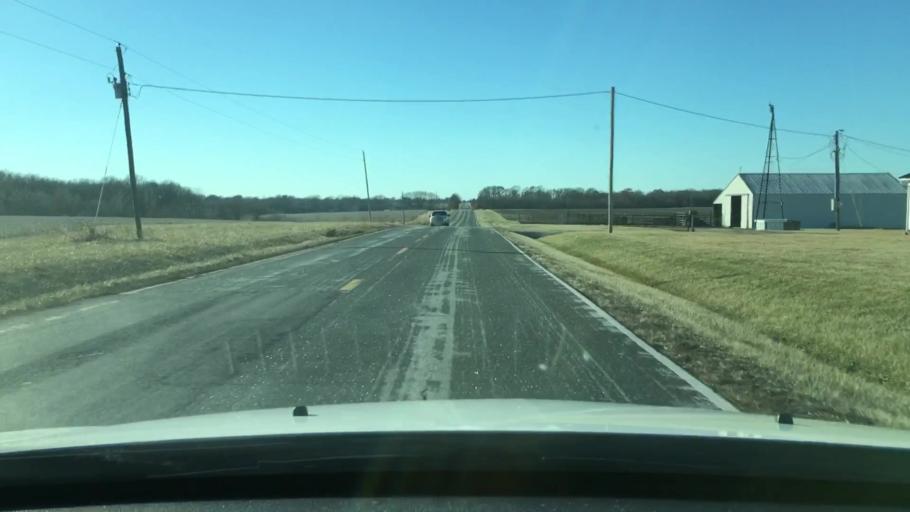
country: US
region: Missouri
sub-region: Audrain County
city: Vandalia
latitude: 39.2812
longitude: -91.6560
